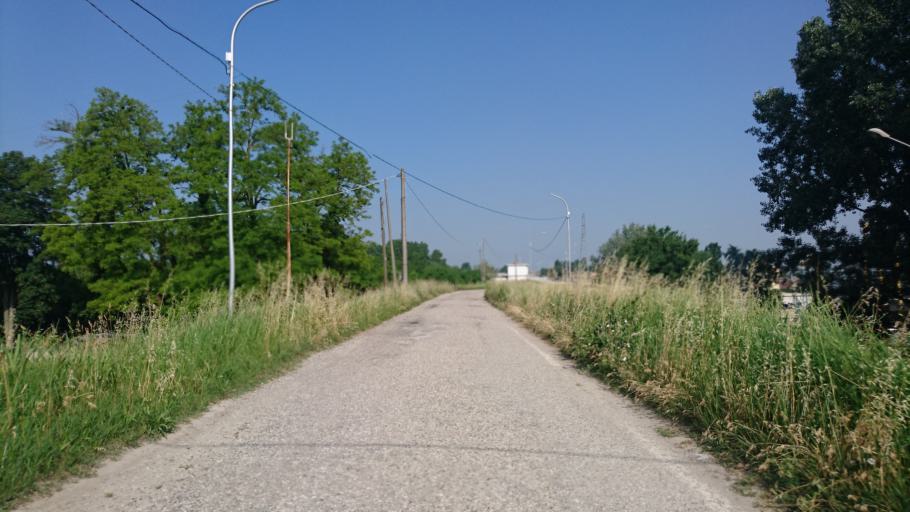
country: IT
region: Lombardy
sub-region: Provincia di Mantova
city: Revere
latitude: 45.0585
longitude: 11.1365
